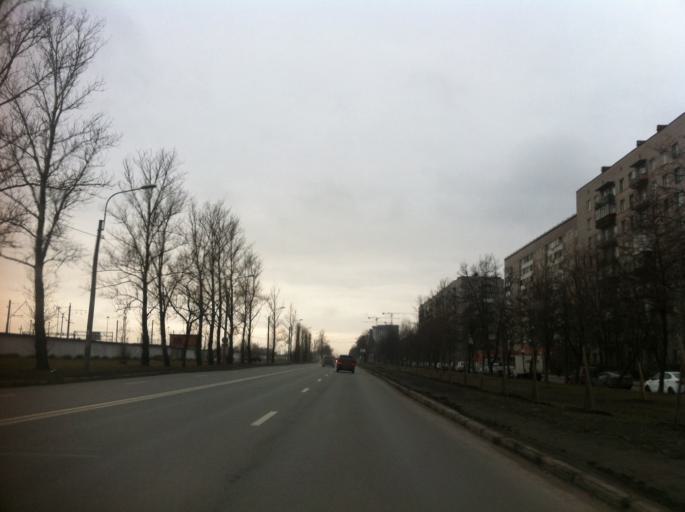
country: RU
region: St.-Petersburg
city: Dachnoye
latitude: 59.8348
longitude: 30.2644
